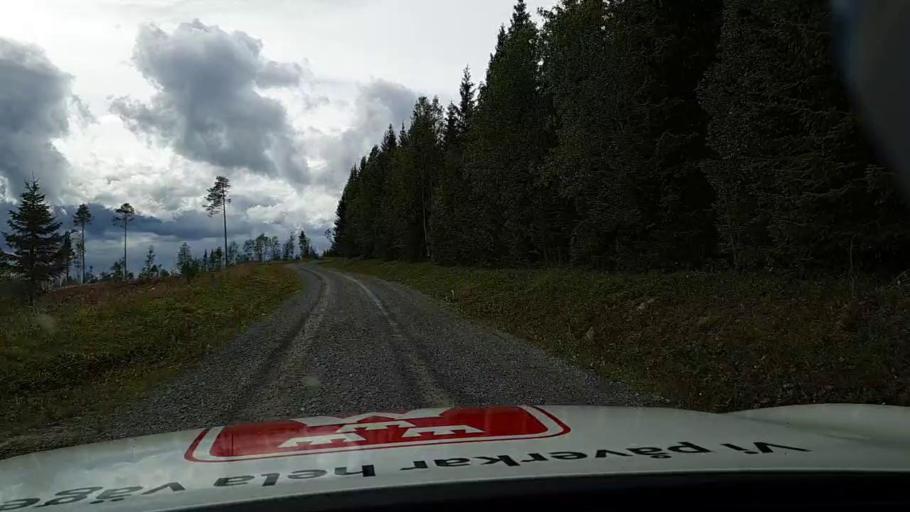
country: SE
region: Jaemtland
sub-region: Krokoms Kommun
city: Valla
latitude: 63.5885
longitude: 14.0016
